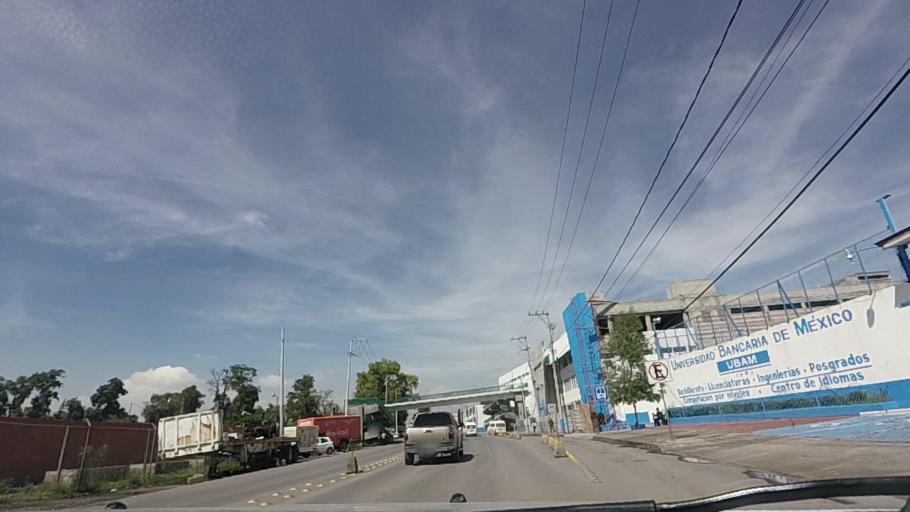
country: MX
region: Mexico
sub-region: Cuautitlan
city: Barrio Tlatenco
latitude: 19.7346
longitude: -99.1841
